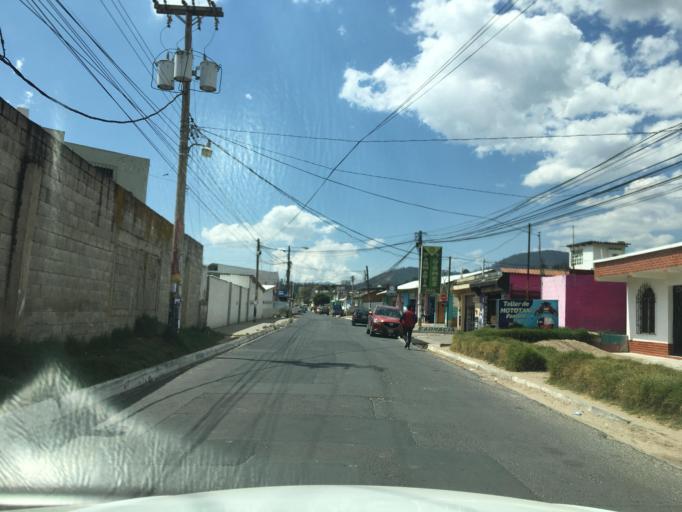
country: GT
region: Totonicapan
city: San Cristobal Totonicapan
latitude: 14.9100
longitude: -91.4503
